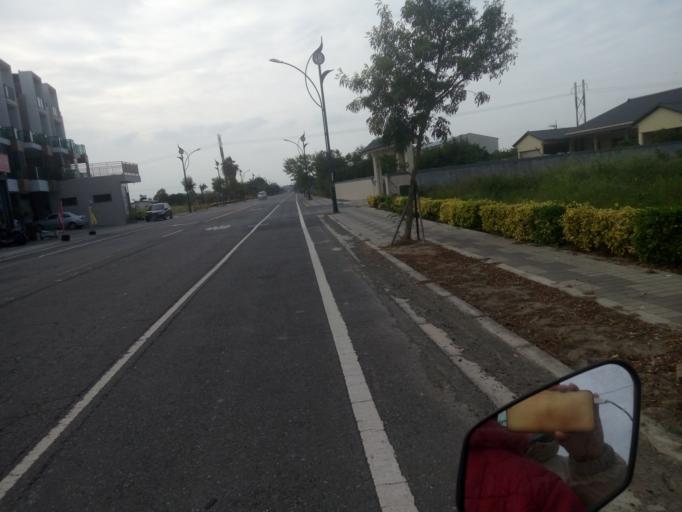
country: TW
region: Taiwan
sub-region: Chiayi
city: Taibao
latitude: 23.4918
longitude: 120.3452
